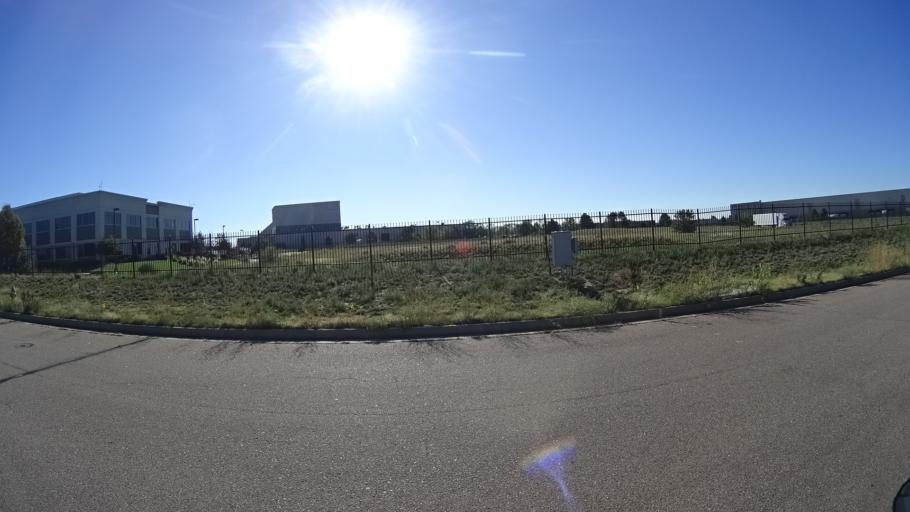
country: US
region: Colorado
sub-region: El Paso County
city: Cimarron Hills
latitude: 38.8163
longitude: -104.7274
